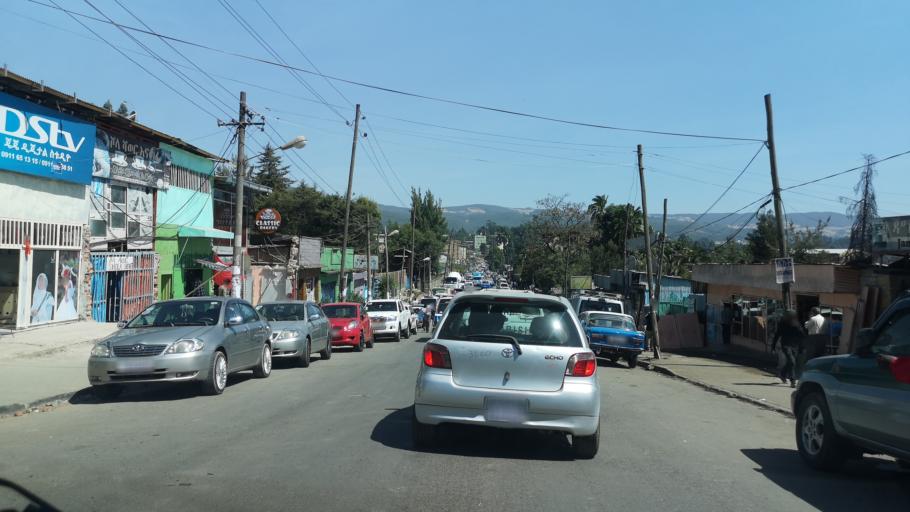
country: ET
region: Adis Abeba
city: Addis Ababa
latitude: 9.0486
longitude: 38.7467
